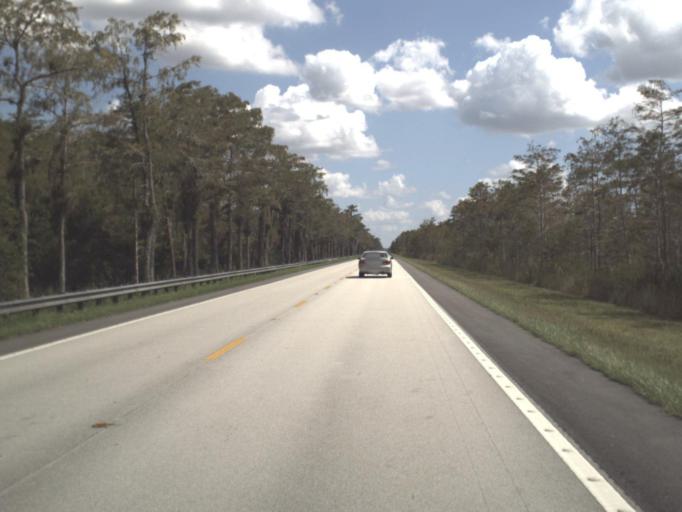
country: US
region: Florida
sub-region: Miami-Dade County
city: Kendall West
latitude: 25.8309
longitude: -80.9028
